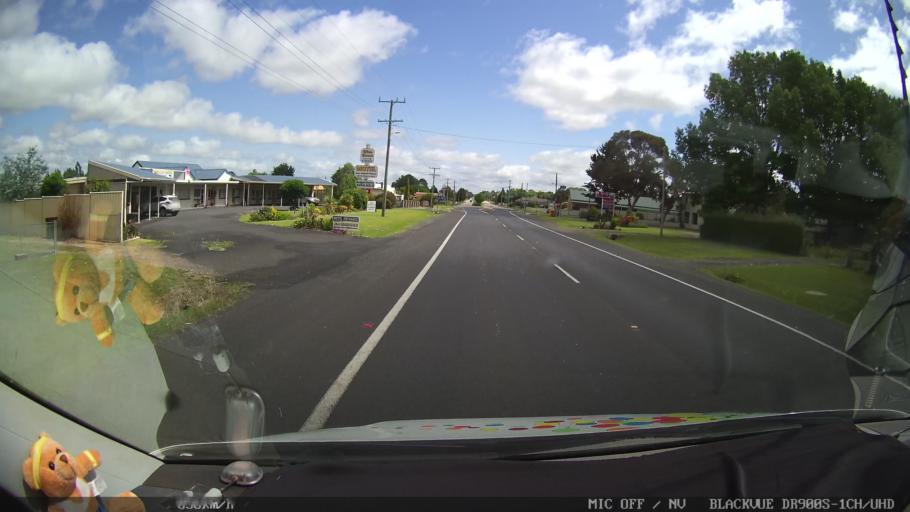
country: AU
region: New South Wales
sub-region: Glen Innes Severn
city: Glen Innes
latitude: -29.7526
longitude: 151.7354
